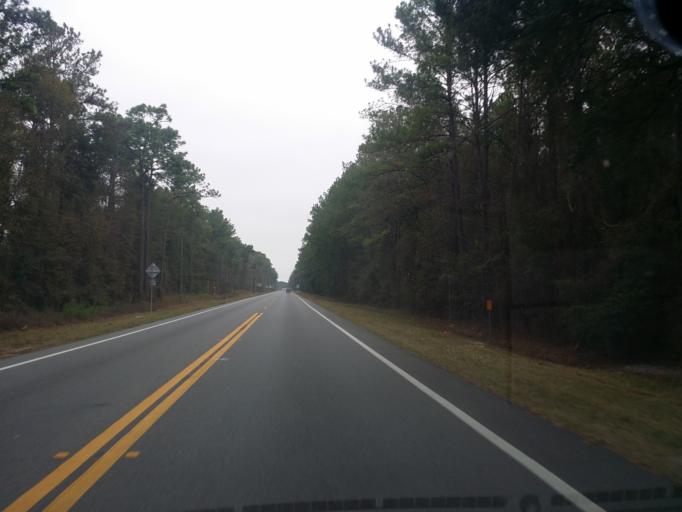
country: US
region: Florida
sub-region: Leon County
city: Woodville
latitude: 30.2994
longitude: -84.3482
